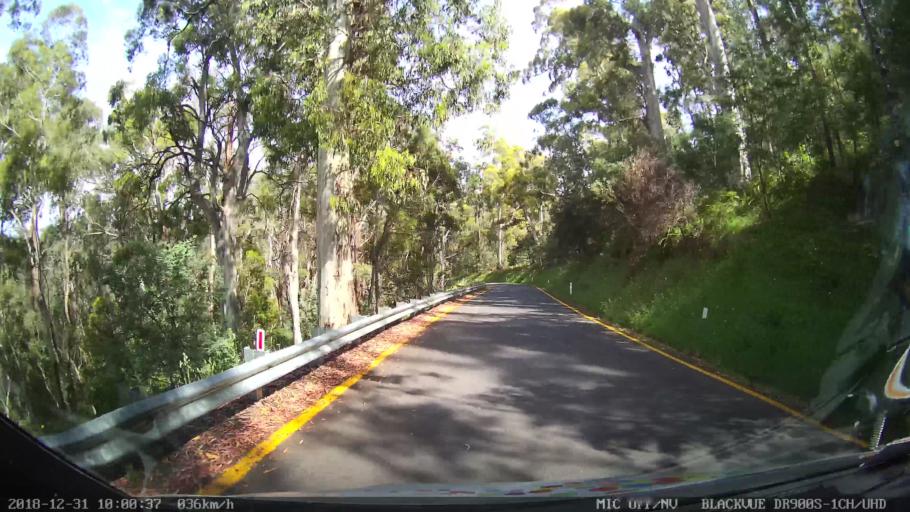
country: AU
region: New South Wales
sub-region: Snowy River
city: Jindabyne
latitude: -36.5316
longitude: 148.2059
